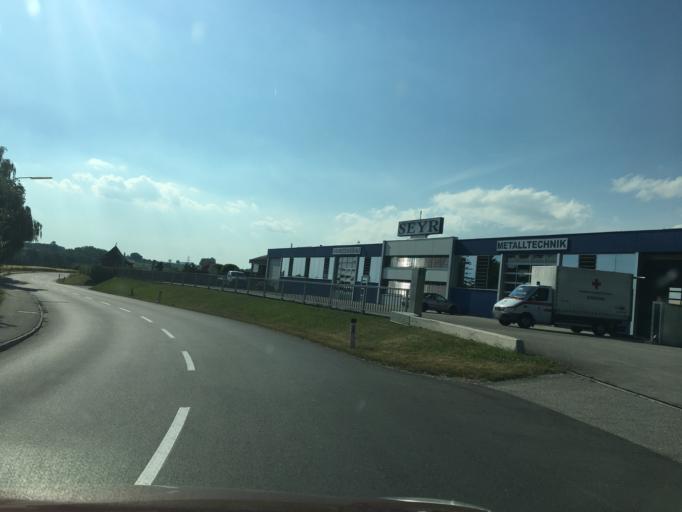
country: AT
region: Lower Austria
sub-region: Politischer Bezirk Amstetten
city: Ennsdorf
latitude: 48.2743
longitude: 14.5212
